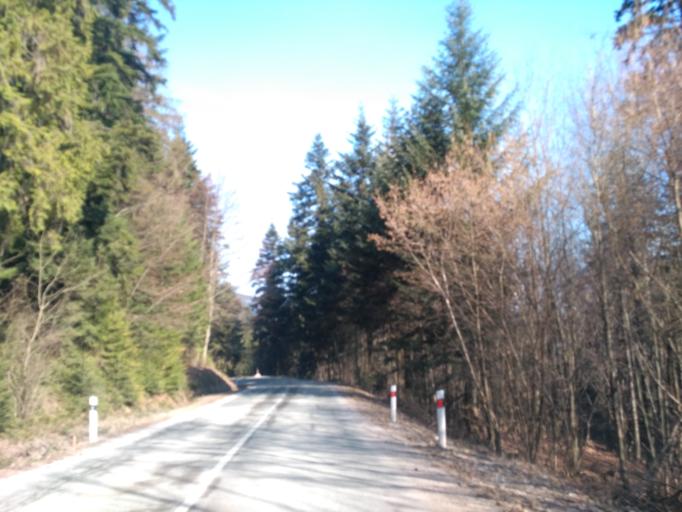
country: SK
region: Kosicky
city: Medzev
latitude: 48.7222
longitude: 20.7510
